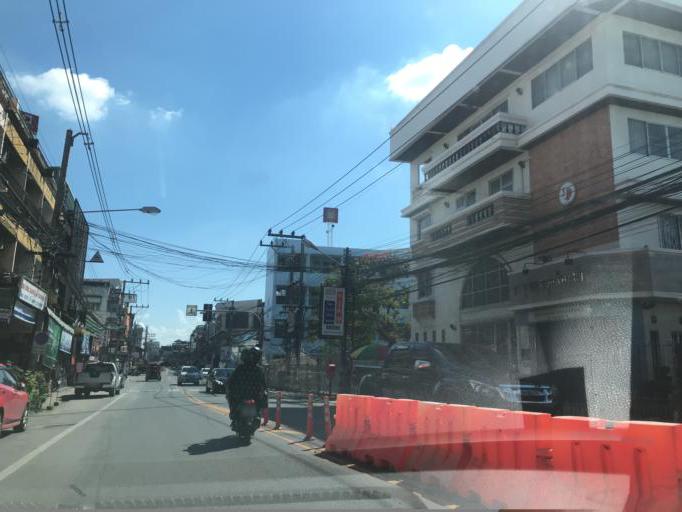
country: TH
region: Chiang Mai
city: Chiang Mai
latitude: 18.7986
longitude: 98.9864
